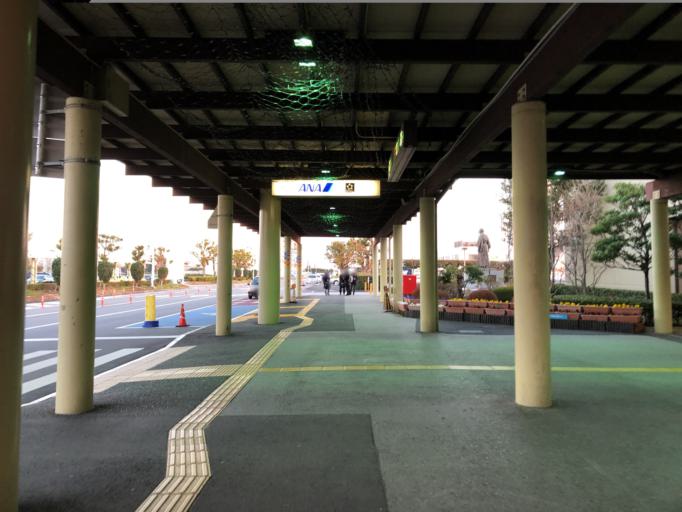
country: JP
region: Kochi
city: Kochi-shi
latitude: 33.5475
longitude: 133.6747
